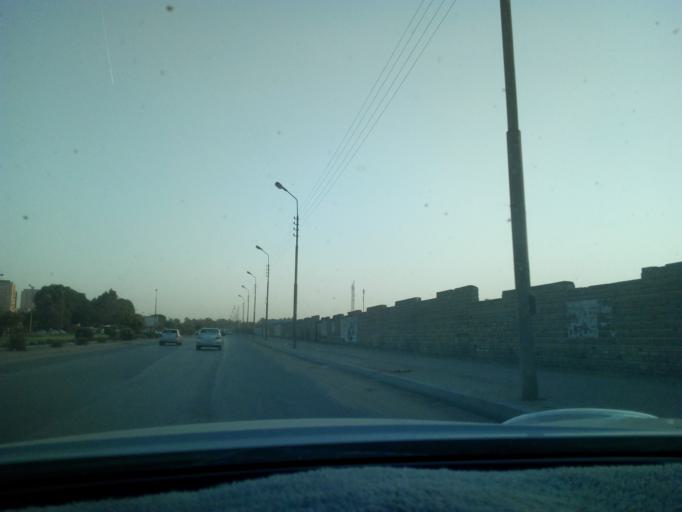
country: EG
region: Muhafazat al Qalyubiyah
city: Al Khankah
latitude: 30.1230
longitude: 31.3632
